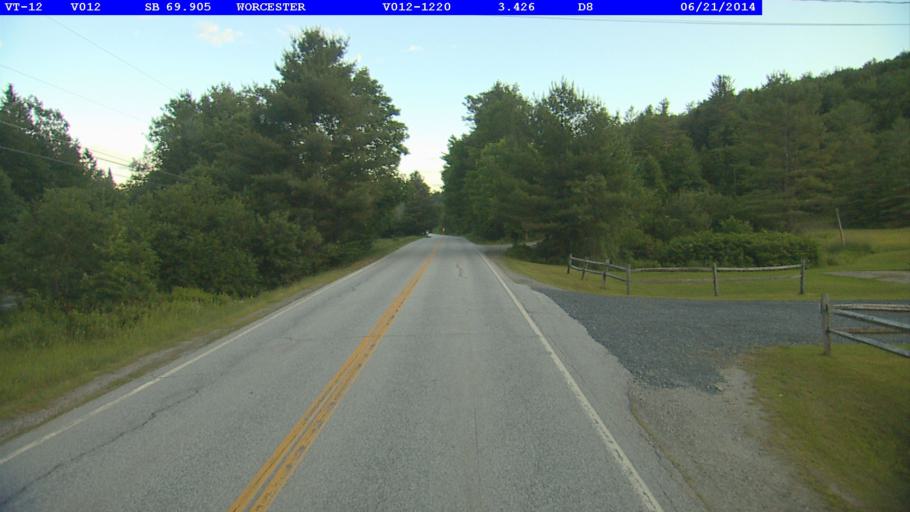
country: US
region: Vermont
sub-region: Washington County
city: Montpelier
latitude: 44.3967
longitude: -72.5561
